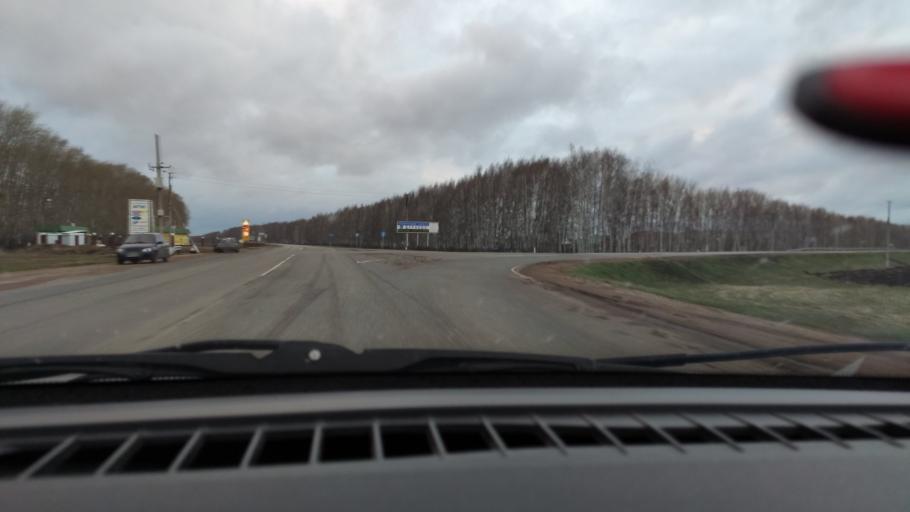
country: RU
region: Bashkortostan
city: Burayevo
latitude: 55.8176
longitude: 55.4229
